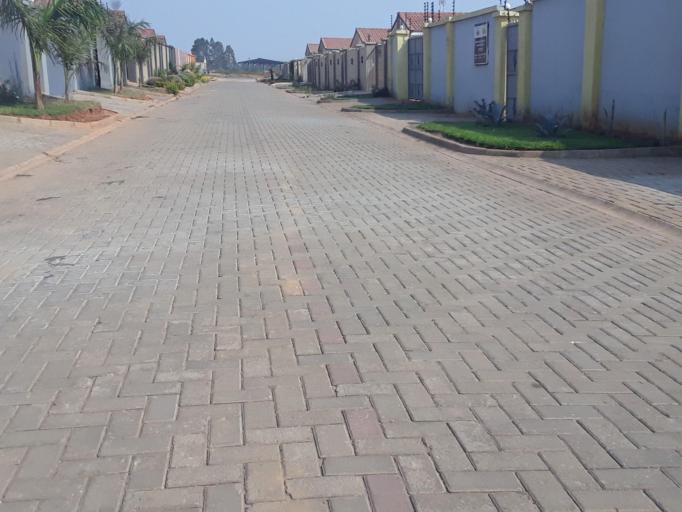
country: ZM
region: Lusaka
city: Lusaka
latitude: -15.3611
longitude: 28.2848
